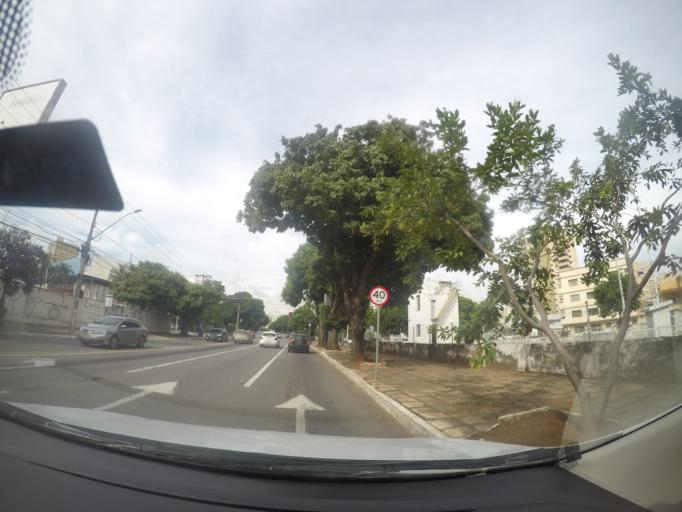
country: BR
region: Goias
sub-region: Goiania
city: Goiania
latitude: -16.6731
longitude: -49.2637
